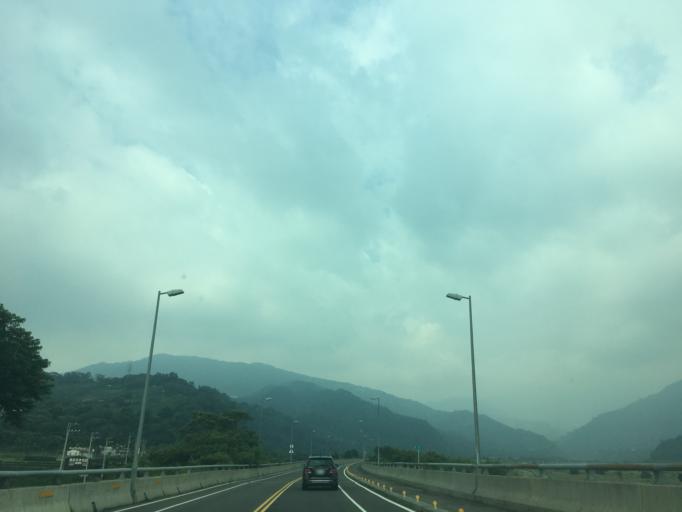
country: TW
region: Taiwan
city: Fengyuan
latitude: 24.2942
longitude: 120.8684
